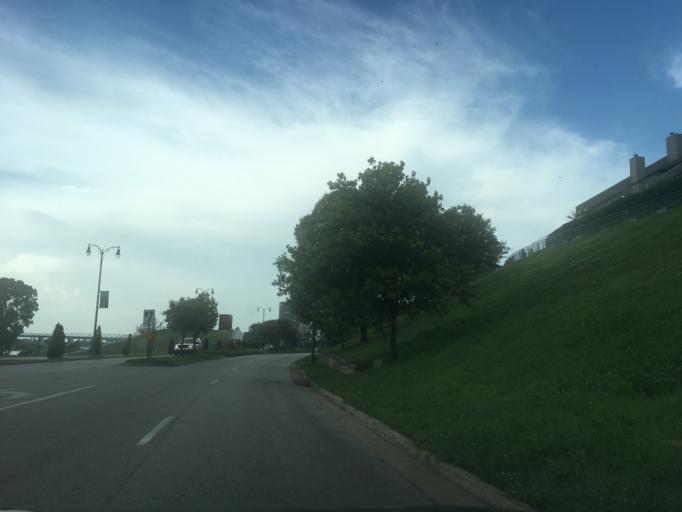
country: US
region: Tennessee
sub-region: Shelby County
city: Memphis
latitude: 35.1383
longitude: -90.0609
